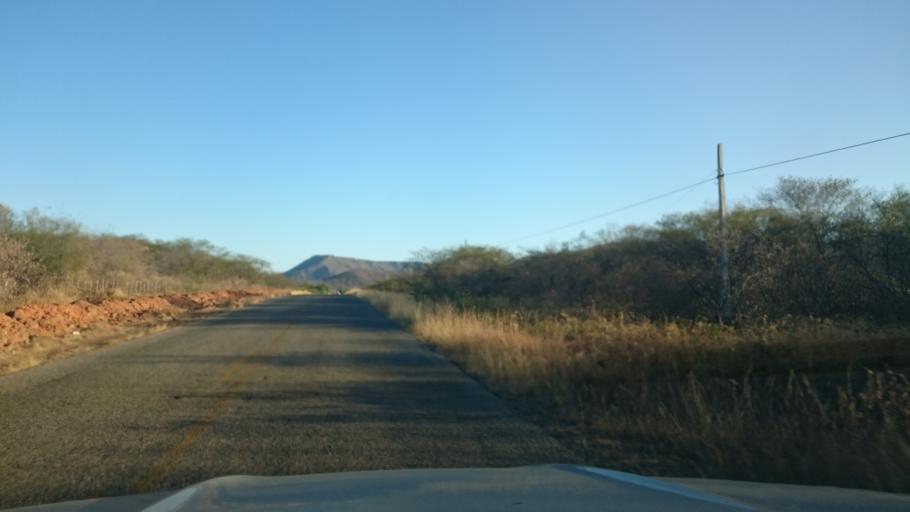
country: BR
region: Rio Grande do Norte
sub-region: Umarizal
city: Umarizal
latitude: -5.9492
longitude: -37.9515
